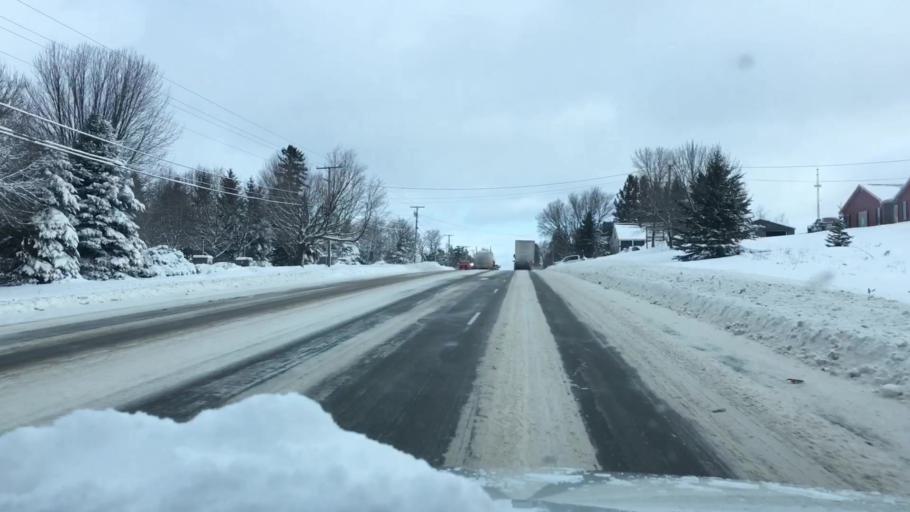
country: US
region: Maine
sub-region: Aroostook County
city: Presque Isle
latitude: 46.7241
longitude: -68.0050
